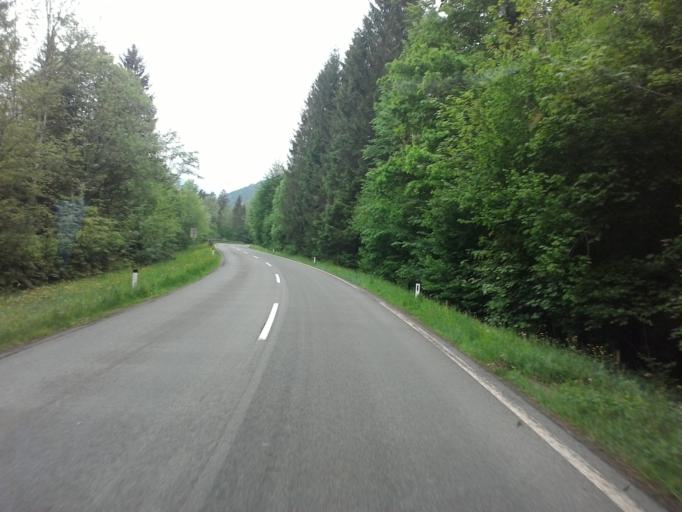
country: AT
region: Styria
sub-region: Politischer Bezirk Liezen
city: Altenmarkt bei Sankt Gallen
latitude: 47.7124
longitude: 14.6820
